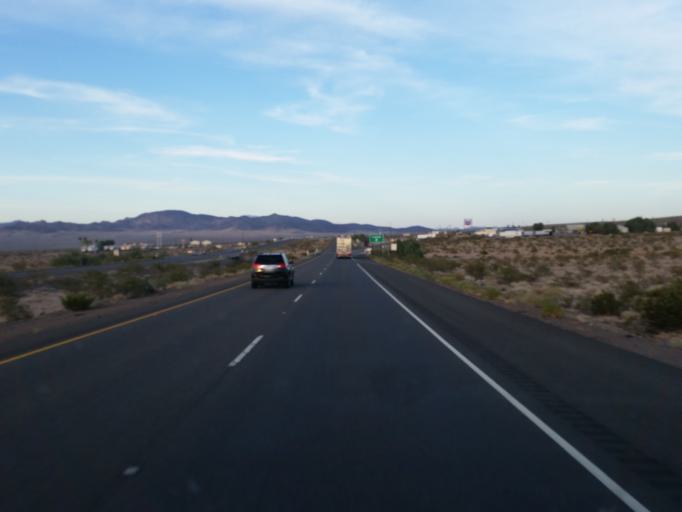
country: US
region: California
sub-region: San Bernardino County
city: Twentynine Palms
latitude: 34.7250
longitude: -116.1705
